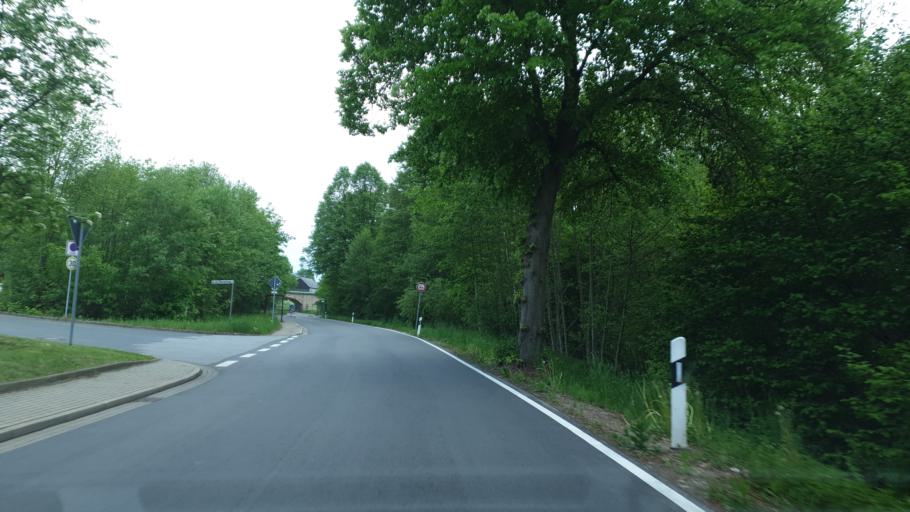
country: DE
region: Saxony
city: Lugau
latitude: 50.7176
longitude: 12.7441
